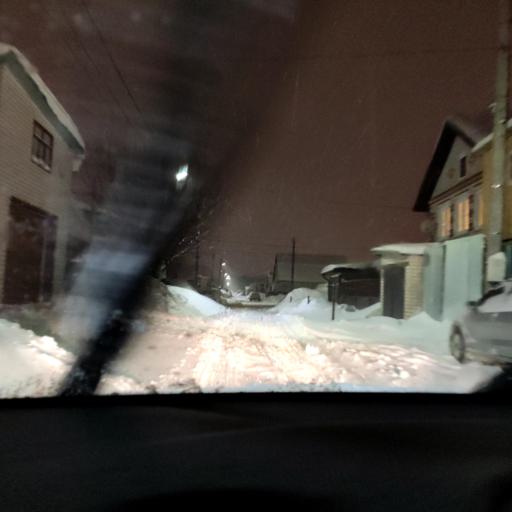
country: RU
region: Tatarstan
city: Staroye Arakchino
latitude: 55.8741
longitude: 49.0231
